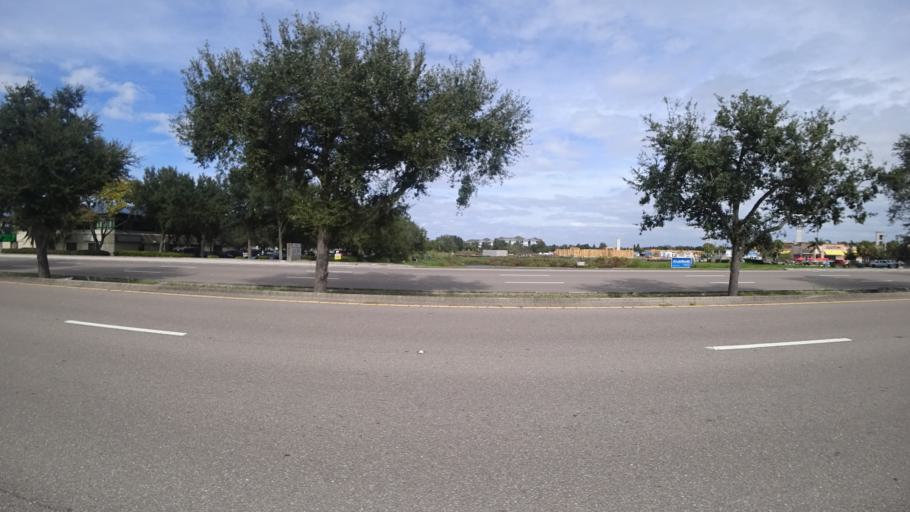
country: US
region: Florida
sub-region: Sarasota County
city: North Sarasota
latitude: 27.3888
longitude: -82.5208
